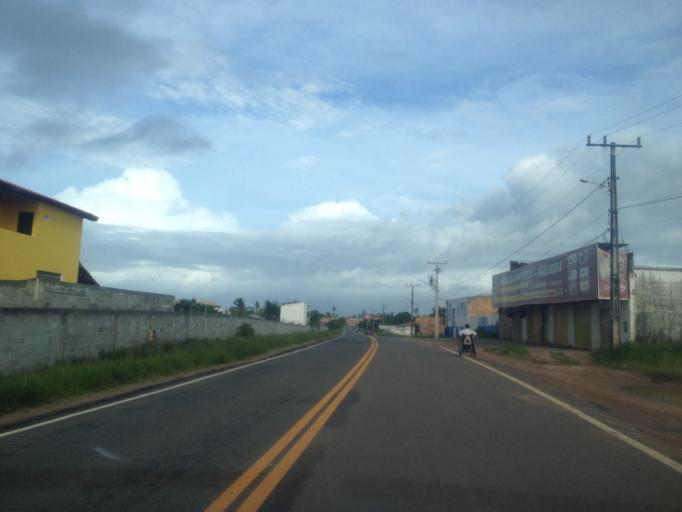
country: BR
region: Bahia
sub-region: Mata De Sao Joao
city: Mata de Sao Joao
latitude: -12.3792
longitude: -37.8847
